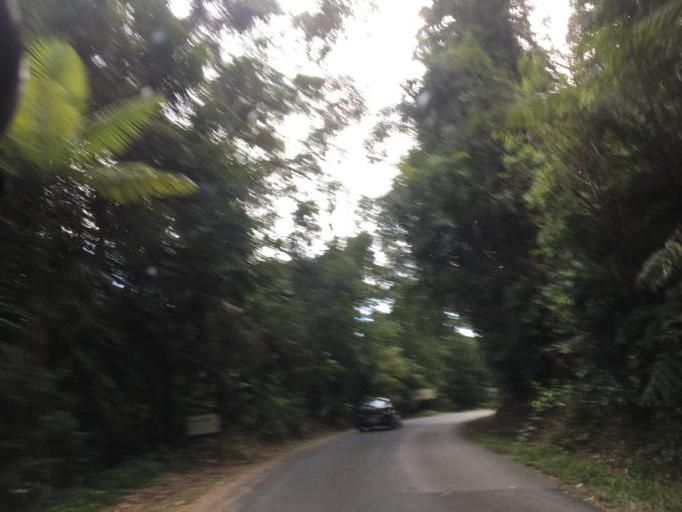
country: AU
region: Queensland
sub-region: Tablelands
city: Kuranda
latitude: -16.8355
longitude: 145.6368
